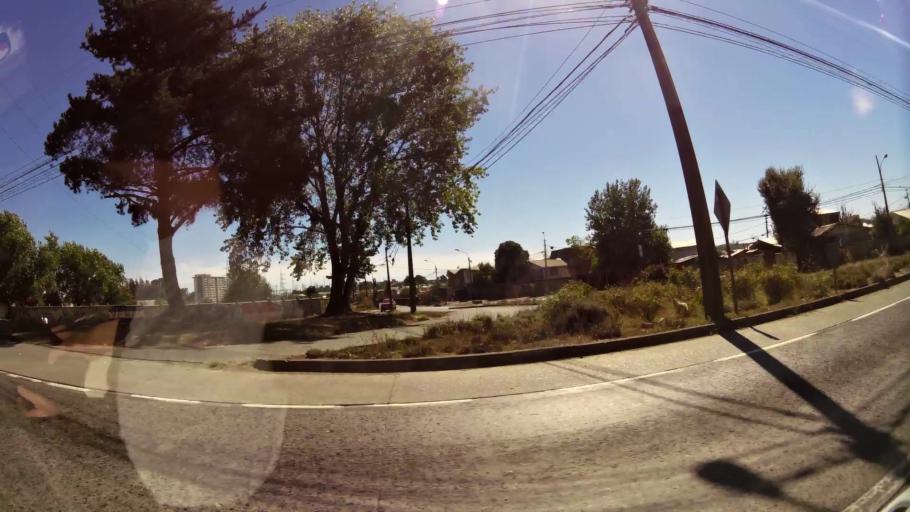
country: CL
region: Biobio
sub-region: Provincia de Concepcion
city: Concepcion
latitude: -36.8017
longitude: -73.0257
